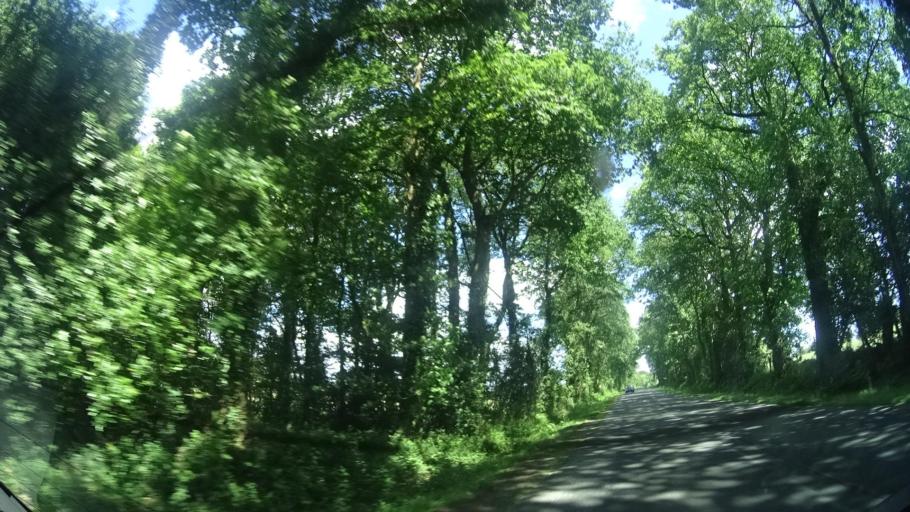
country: FR
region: Brittany
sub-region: Departement du Morbihan
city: Pluherlin
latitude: 47.6783
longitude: -2.3874
